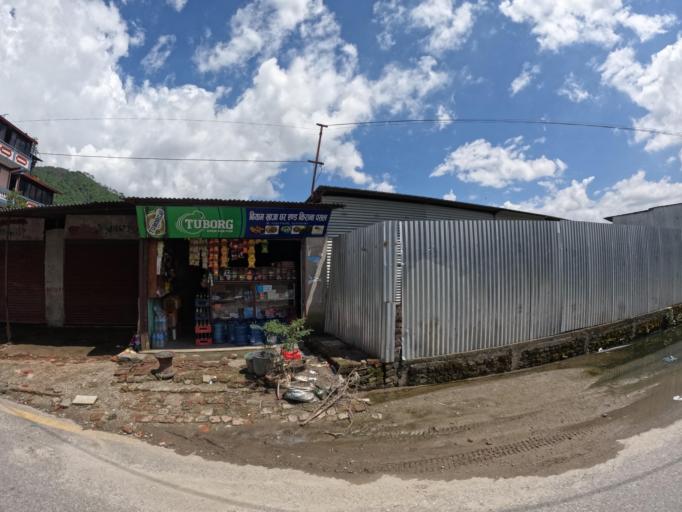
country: NP
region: Central Region
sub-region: Bagmati Zone
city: Kathmandu
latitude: 27.7832
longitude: 85.3256
